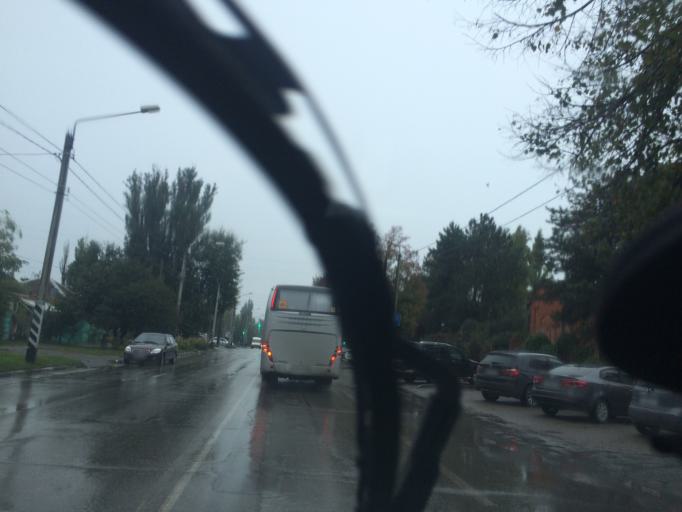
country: RU
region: Rostov
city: Azov
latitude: 47.0953
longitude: 39.4469
